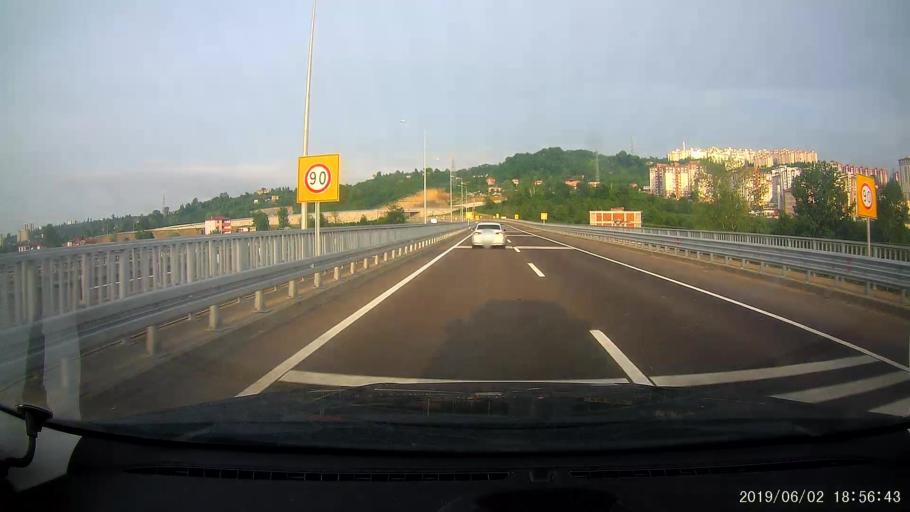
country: TR
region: Ordu
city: Ordu
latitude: 40.9542
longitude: 37.8977
